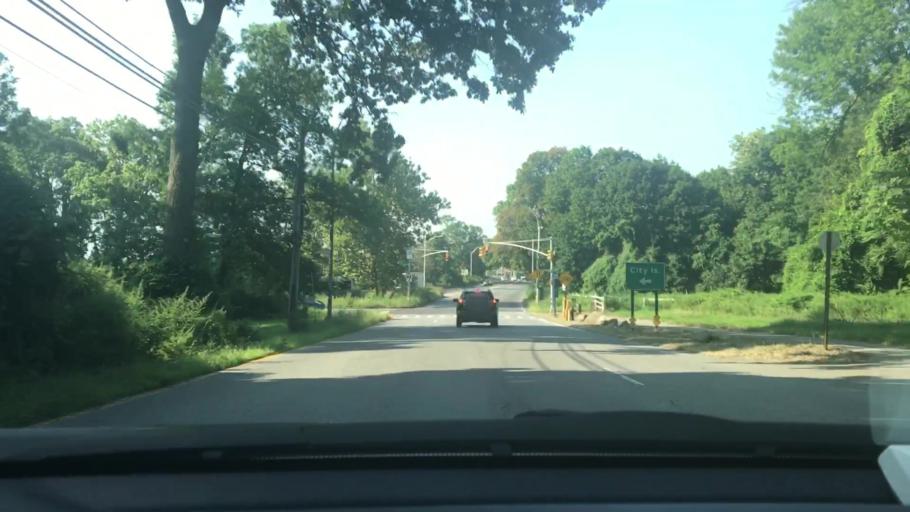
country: US
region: New York
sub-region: Bronx
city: Eastchester
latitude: 40.8654
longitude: -73.8136
